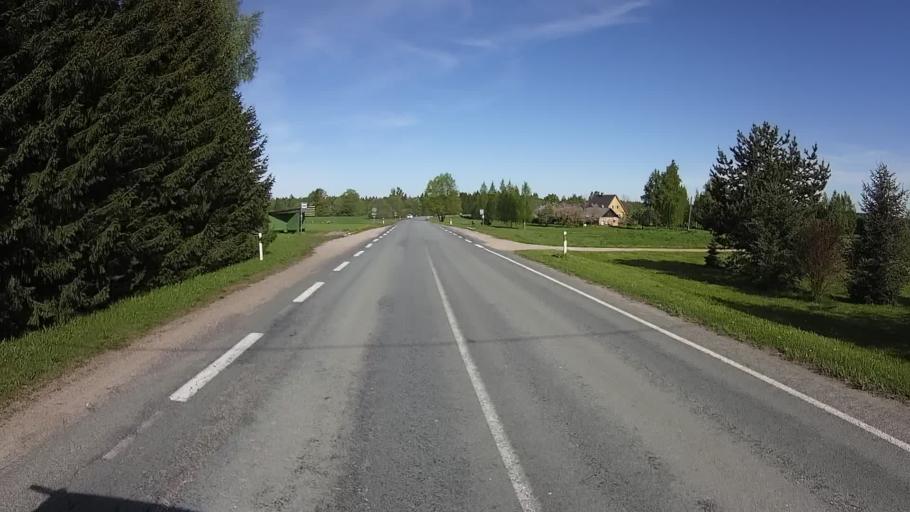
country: EE
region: Polvamaa
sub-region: Polva linn
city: Polva
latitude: 58.2264
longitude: 27.0287
